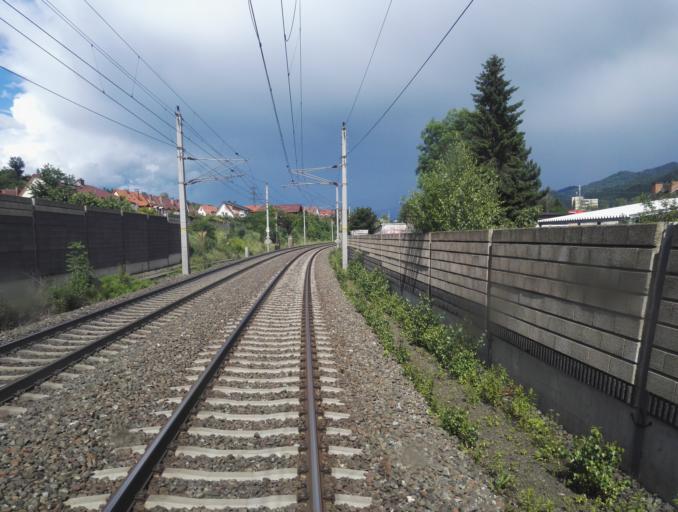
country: AT
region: Styria
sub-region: Politischer Bezirk Bruck-Muerzzuschlag
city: Kapfenberg
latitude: 47.4501
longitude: 15.3063
